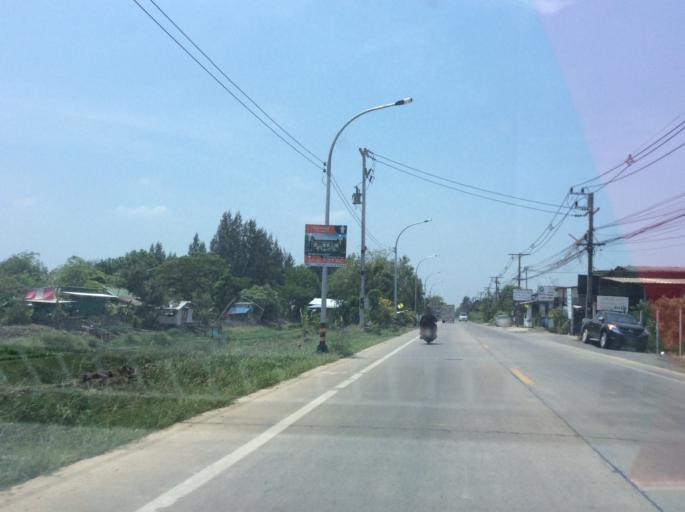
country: TH
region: Pathum Thani
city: Ban Rangsit
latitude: 14.0251
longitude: 100.7786
